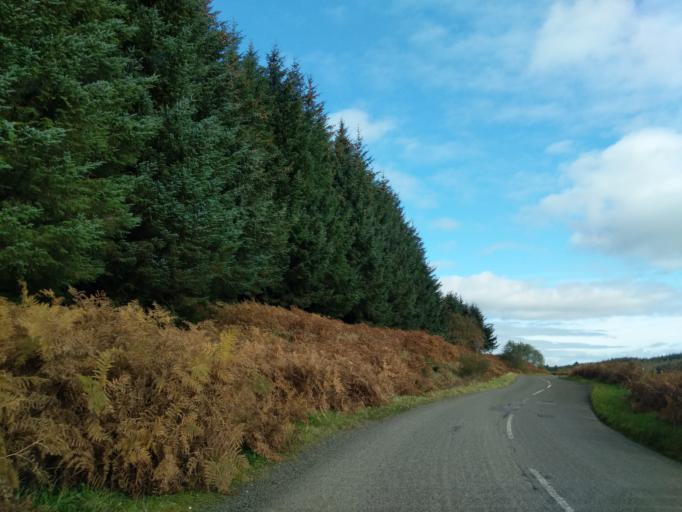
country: GB
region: Scotland
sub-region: Dumfries and Galloway
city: Castle Douglas
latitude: 55.1461
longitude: -4.0340
